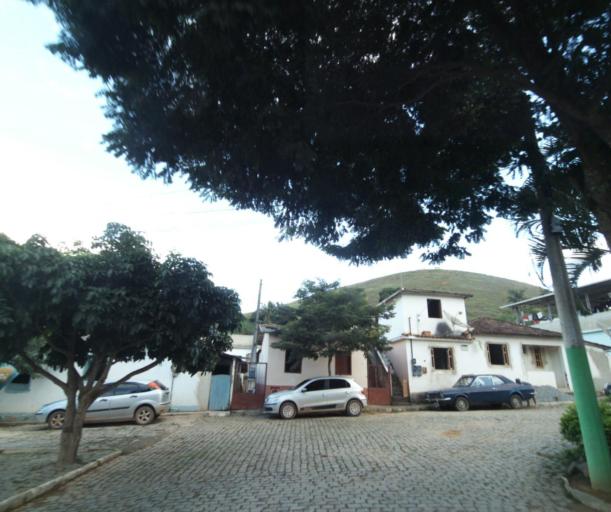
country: BR
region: Espirito Santo
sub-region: Guacui
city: Guacui
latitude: -20.6212
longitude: -41.6848
